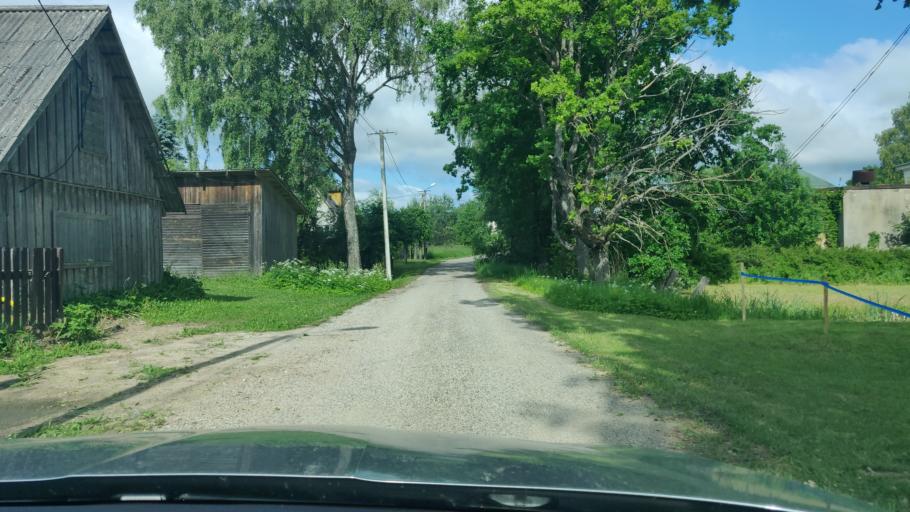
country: EE
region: Vorumaa
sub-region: Voru linn
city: Voru
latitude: 57.7304
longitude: 27.2845
